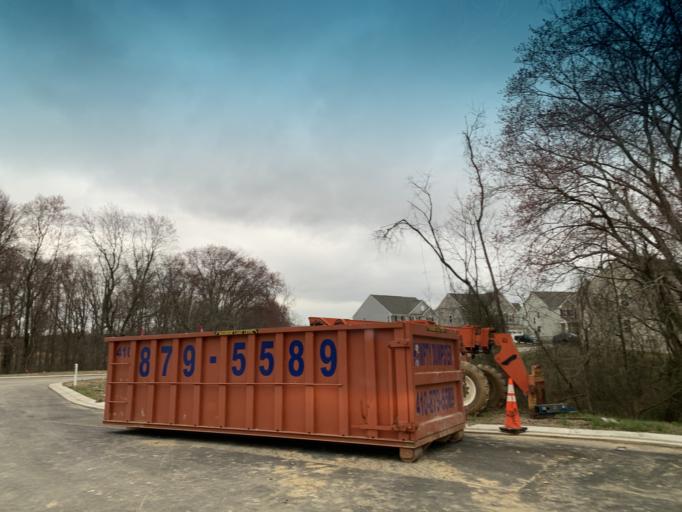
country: US
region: Maryland
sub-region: Harford County
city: Aberdeen
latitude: 39.5427
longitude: -76.1910
